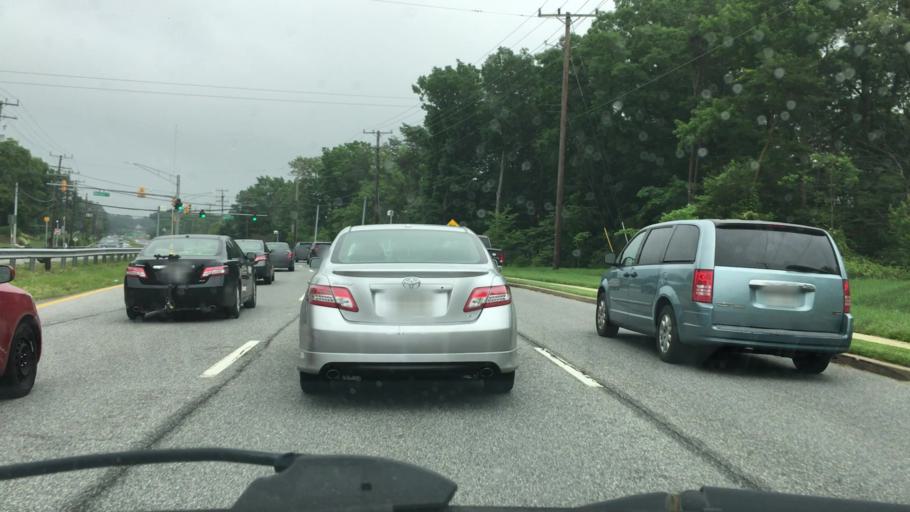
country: US
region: Maryland
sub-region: Prince George's County
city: Goddard
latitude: 38.9918
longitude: -76.8656
